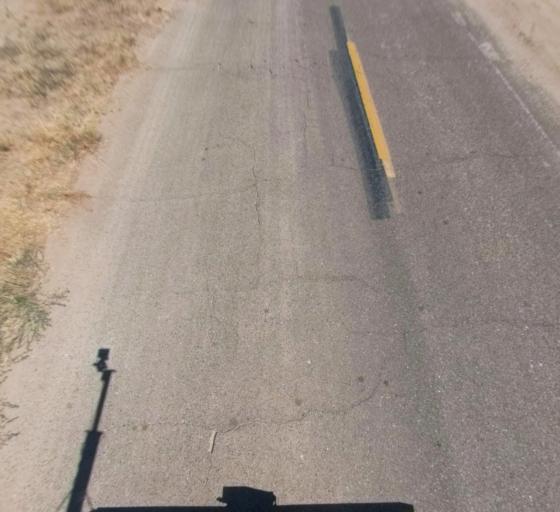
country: US
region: California
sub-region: Fresno County
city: Biola
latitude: 36.8501
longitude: -120.0192
